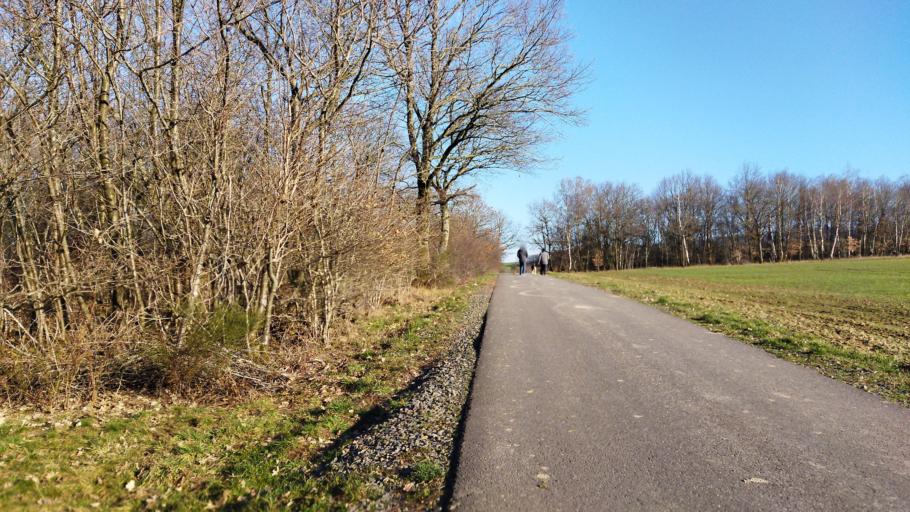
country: DE
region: Rheinland-Pfalz
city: Selchenbach
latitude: 49.4981
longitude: 7.2864
